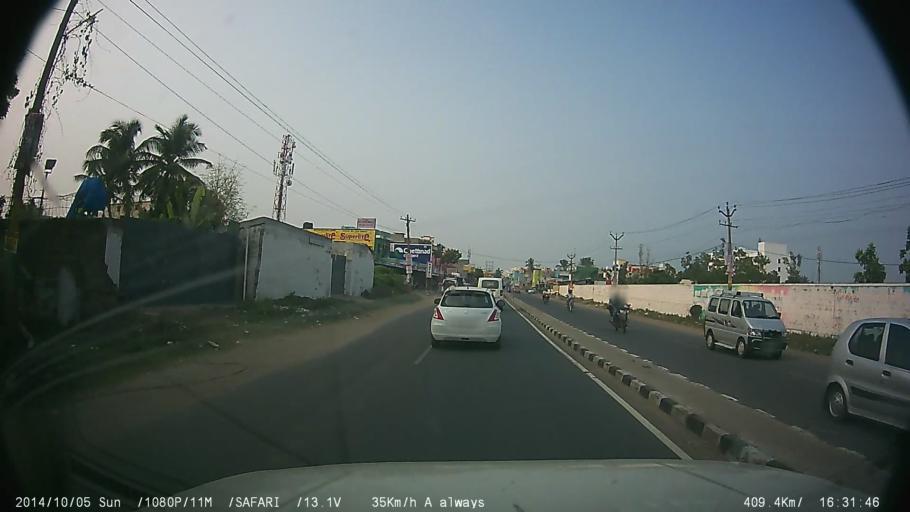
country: IN
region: Tamil Nadu
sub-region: Kancheepuram
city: Vengavasal
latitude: 12.8016
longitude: 80.2236
